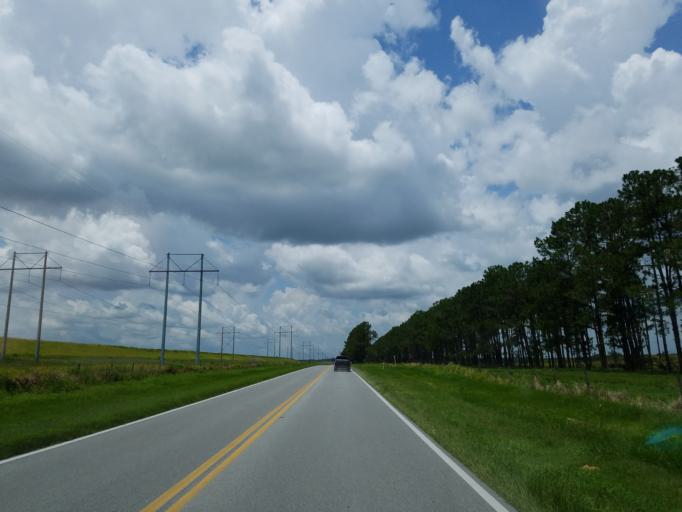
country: US
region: Florida
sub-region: Polk County
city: Mulberry
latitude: 27.8509
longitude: -82.0072
